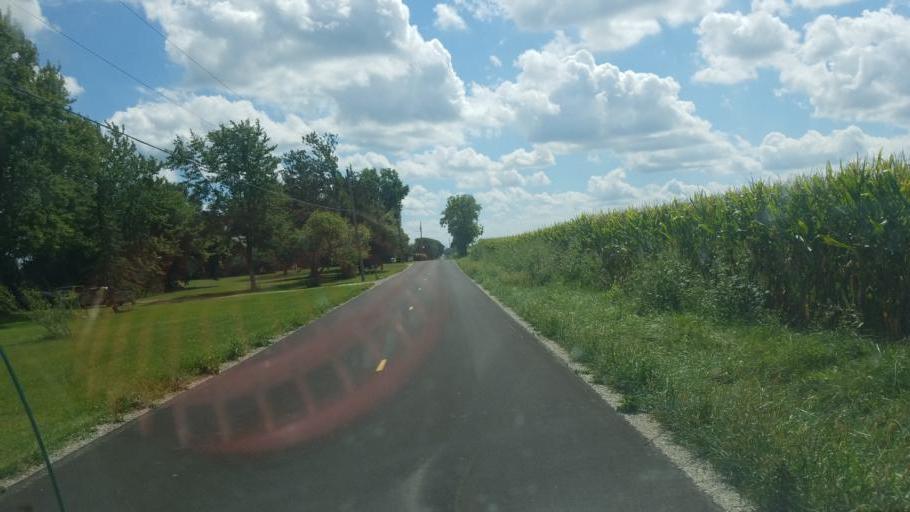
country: US
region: Ohio
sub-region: Marion County
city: Prospect
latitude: 40.5079
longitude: -83.1658
